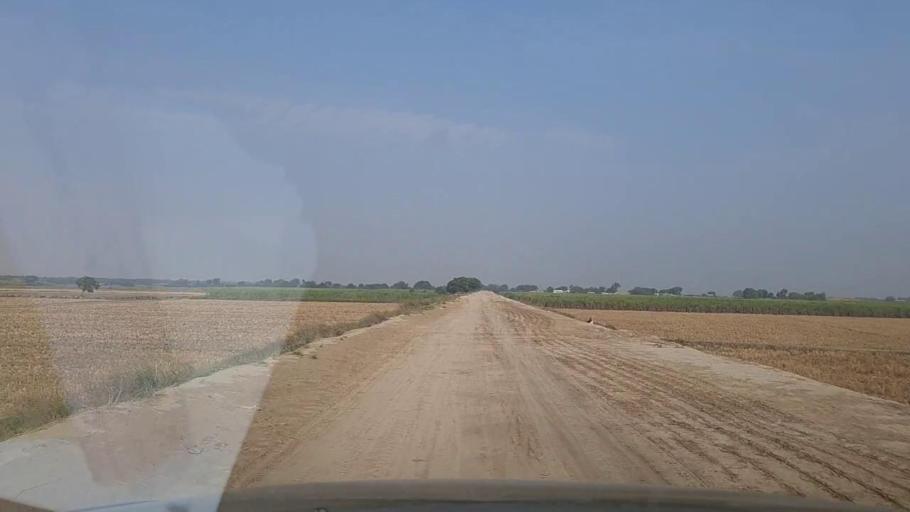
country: PK
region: Sindh
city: Bulri
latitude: 25.0172
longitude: 68.2843
